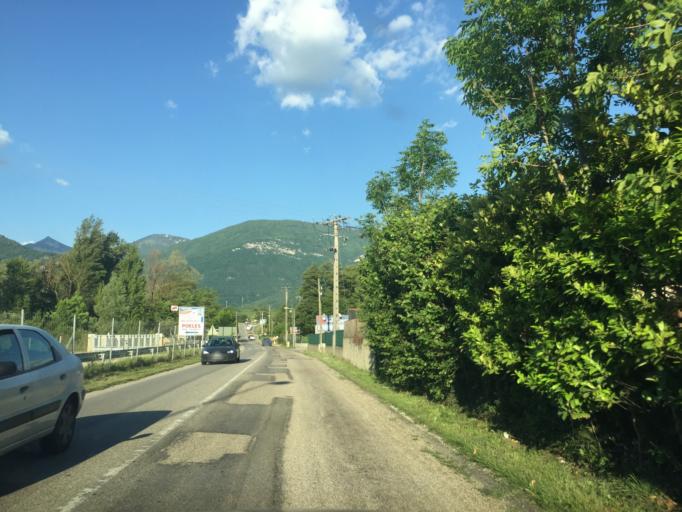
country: FR
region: Rhone-Alpes
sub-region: Departement de la Savoie
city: Saint-Baldoph
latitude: 45.5362
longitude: 5.9606
